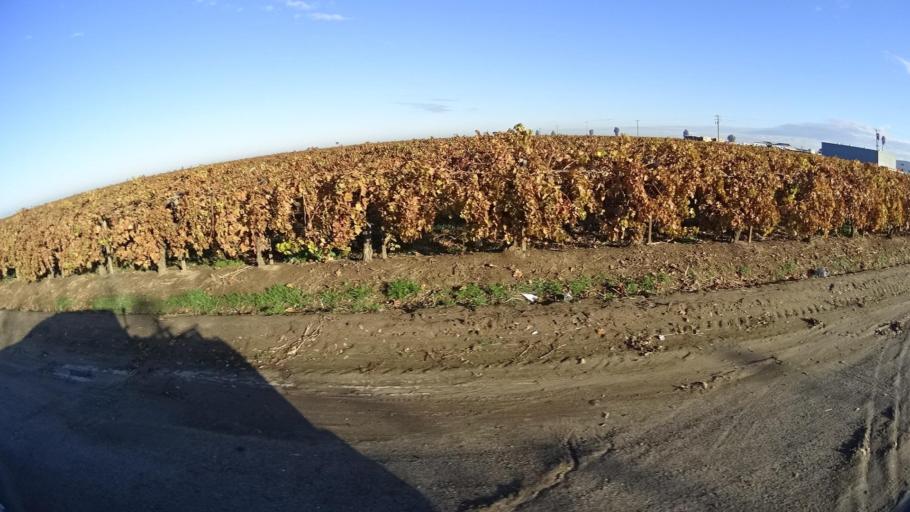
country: US
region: California
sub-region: Kern County
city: Delano
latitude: 35.7904
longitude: -119.2601
